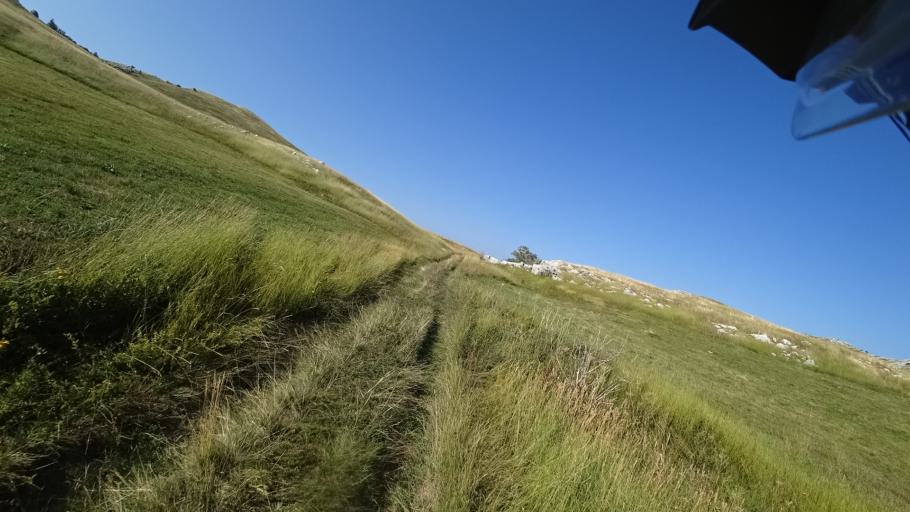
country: HR
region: Sibensko-Kniniska
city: Knin
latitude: 44.2029
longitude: 16.1417
